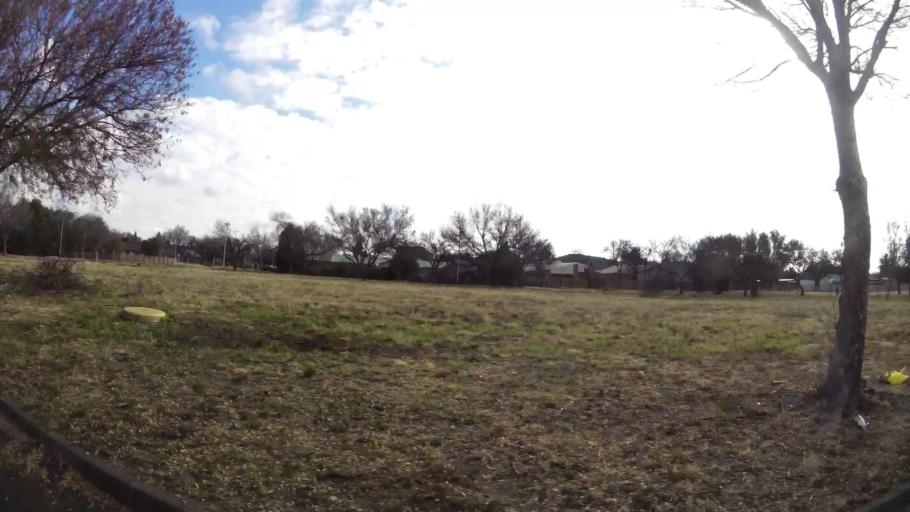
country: ZA
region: Orange Free State
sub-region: Mangaung Metropolitan Municipality
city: Bloemfontein
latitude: -29.0842
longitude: 26.2395
